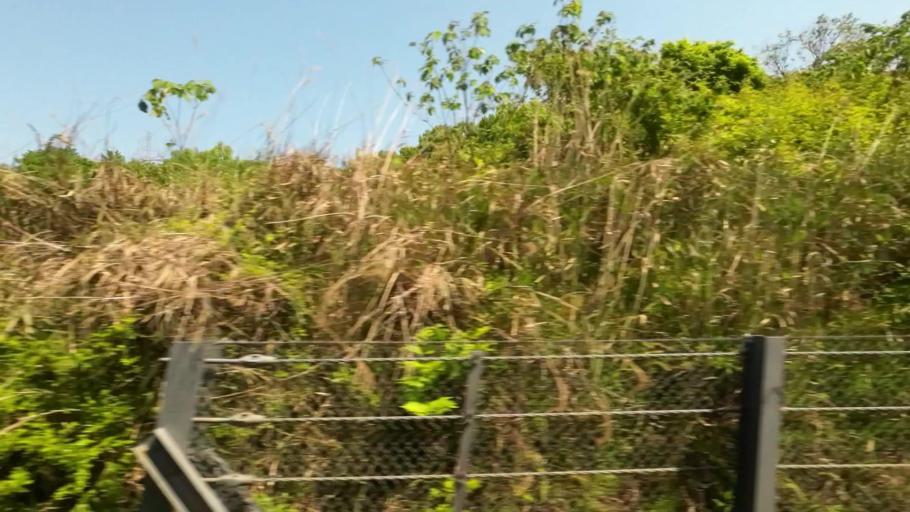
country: JP
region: Ehime
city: Saijo
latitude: 33.9223
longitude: 133.2409
